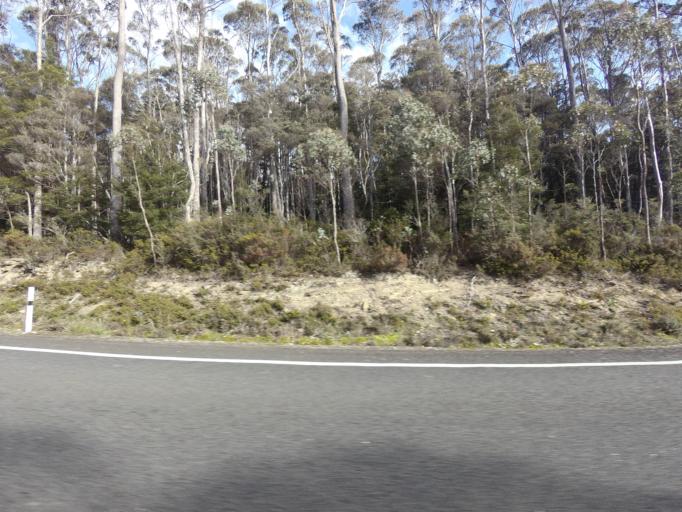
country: AU
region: Tasmania
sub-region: Meander Valley
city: Deloraine
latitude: -41.7075
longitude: 146.7212
